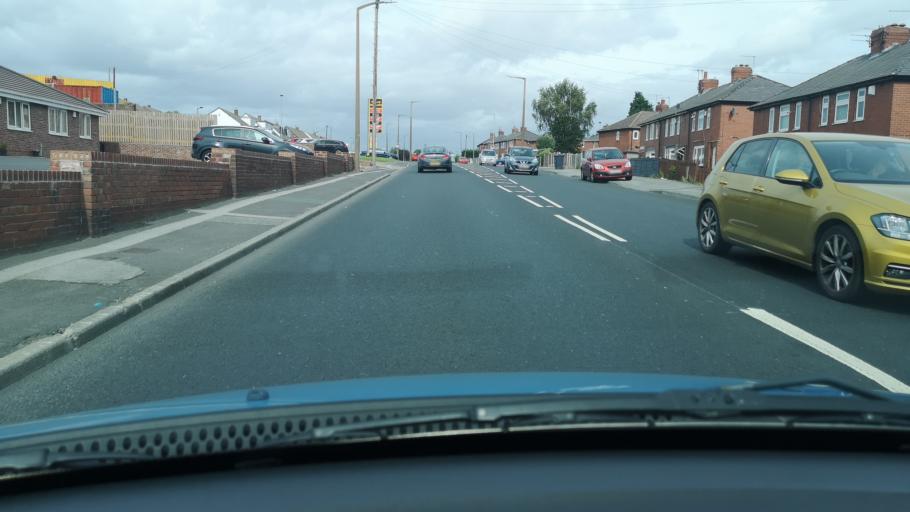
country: GB
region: England
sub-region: Barnsley
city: Cudworth
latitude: 53.5624
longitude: -1.4355
